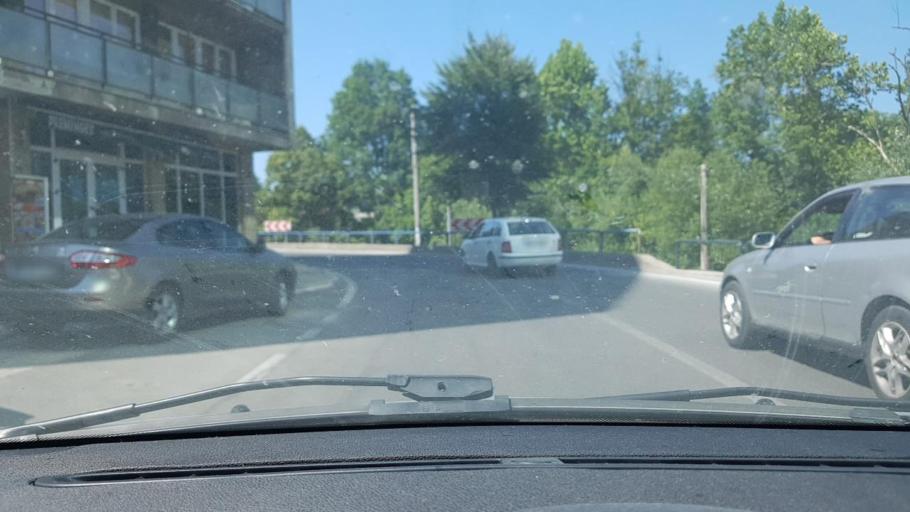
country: BA
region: Federation of Bosnia and Herzegovina
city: Bihac
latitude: 44.8160
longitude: 15.8707
